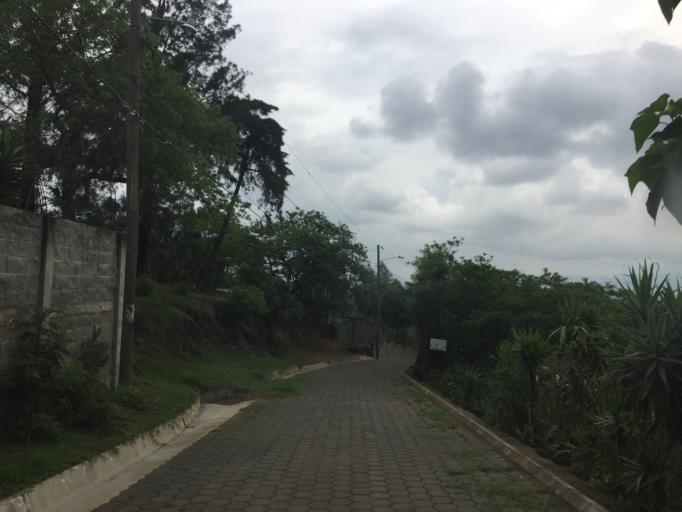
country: GT
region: Guatemala
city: Amatitlan
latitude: 14.5068
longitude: -90.6491
